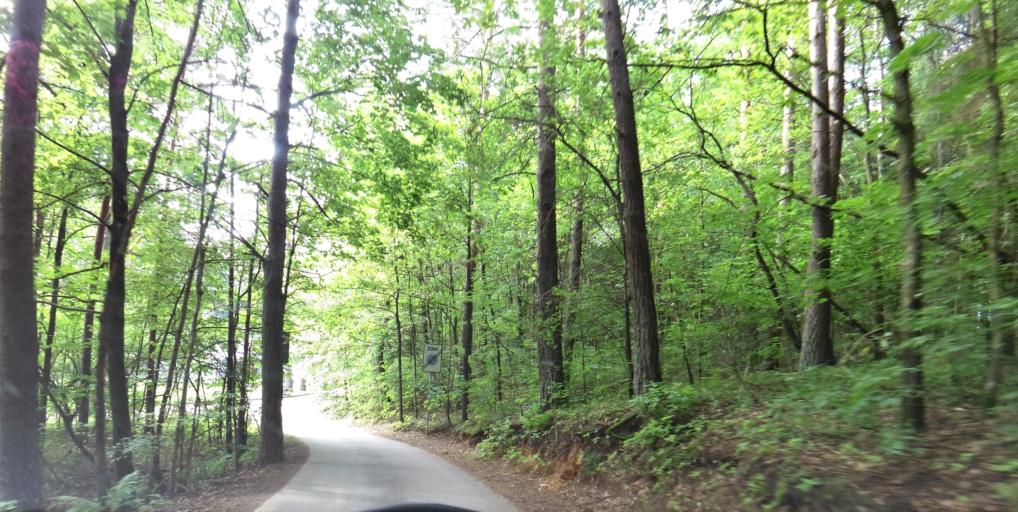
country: LT
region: Vilnius County
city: Seskine
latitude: 54.7319
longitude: 25.2840
